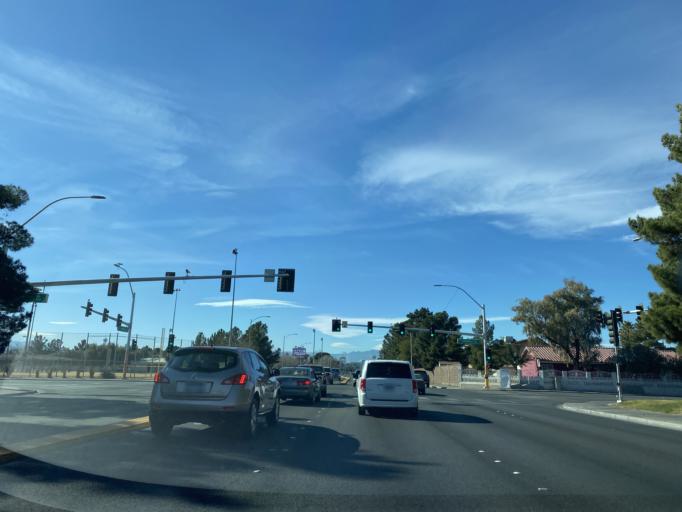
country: US
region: Nevada
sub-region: Clark County
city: North Las Vegas
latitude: 36.1735
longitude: -115.0889
